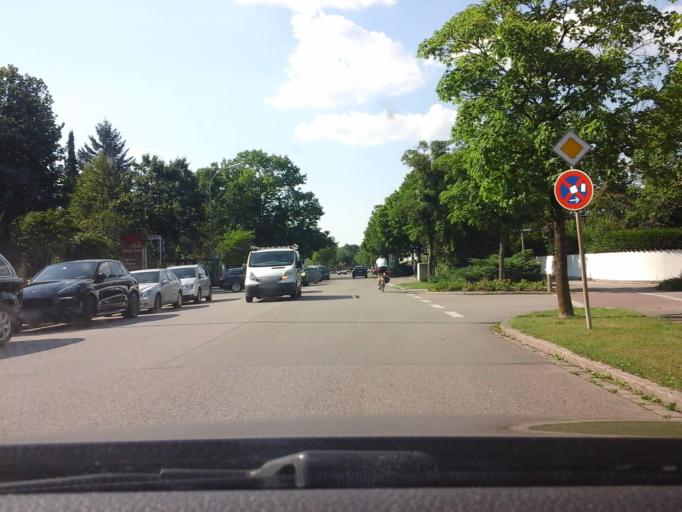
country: DE
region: Bavaria
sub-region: Upper Bavaria
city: Unterhaching
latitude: 48.0708
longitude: 11.6071
